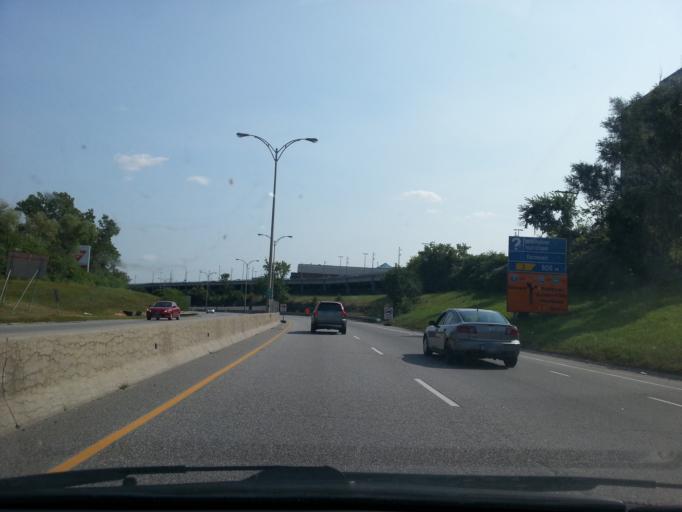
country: CA
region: Quebec
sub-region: Outaouais
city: Gatineau
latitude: 45.4444
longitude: -75.7315
